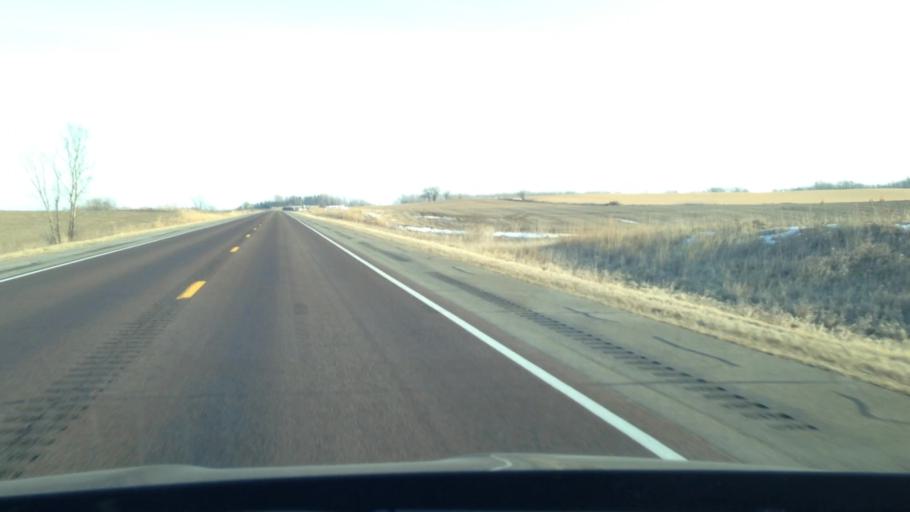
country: US
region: Minnesota
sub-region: Goodhue County
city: Goodhue
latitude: 44.4313
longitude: -92.6181
